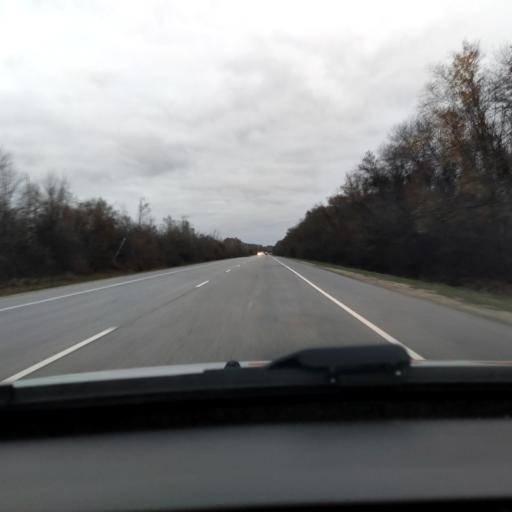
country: RU
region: Lipetsk
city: Borinskoye
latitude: 52.3624
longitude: 39.2021
